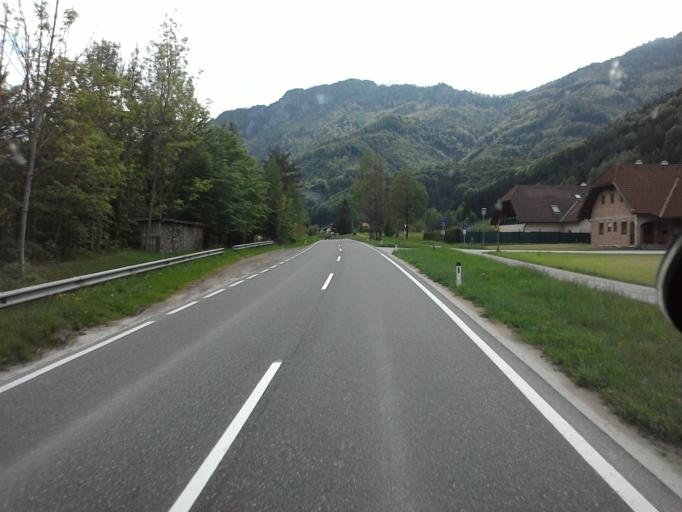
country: AT
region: Upper Austria
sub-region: Politischer Bezirk Kirchdorf an der Krems
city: Micheldorf in Oberoesterreich
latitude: 47.8391
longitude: 14.1623
